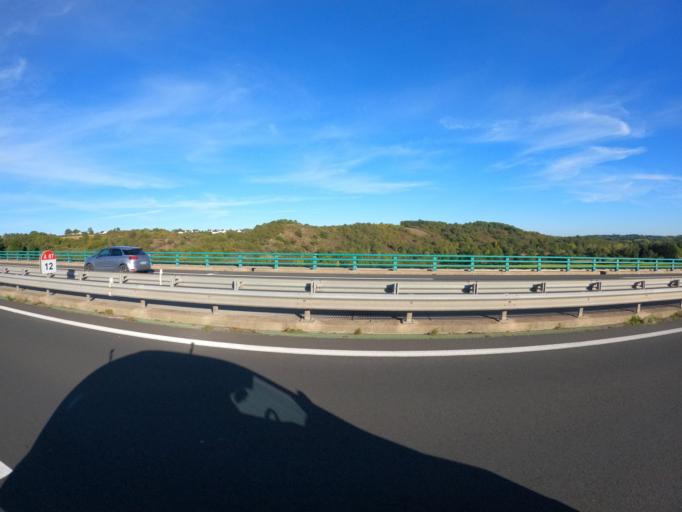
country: FR
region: Pays de la Loire
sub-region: Departement de Maine-et-Loire
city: Beaulieu-sur-Layon
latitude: 47.3107
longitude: -0.6073
